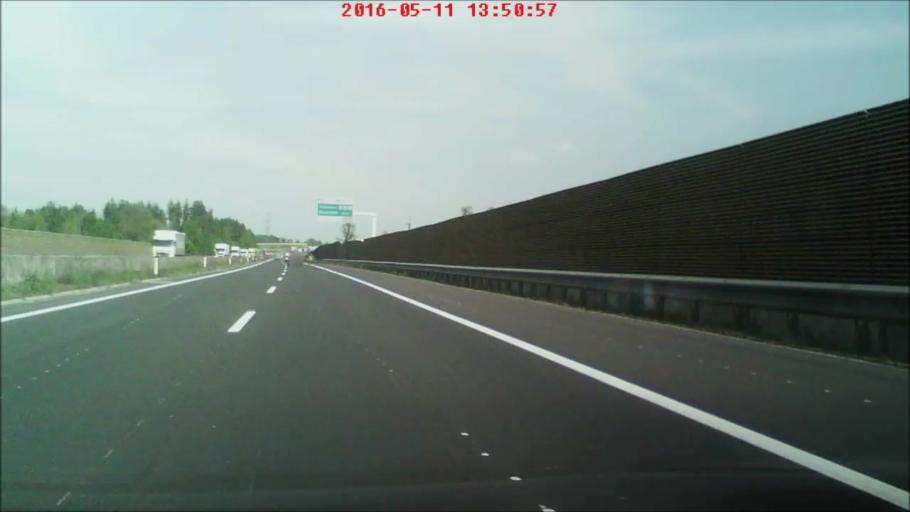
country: AT
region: Upper Austria
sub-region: Politischer Bezirk Vocklabruck
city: Wolfsegg am Hausruck
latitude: 48.1751
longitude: 13.7132
